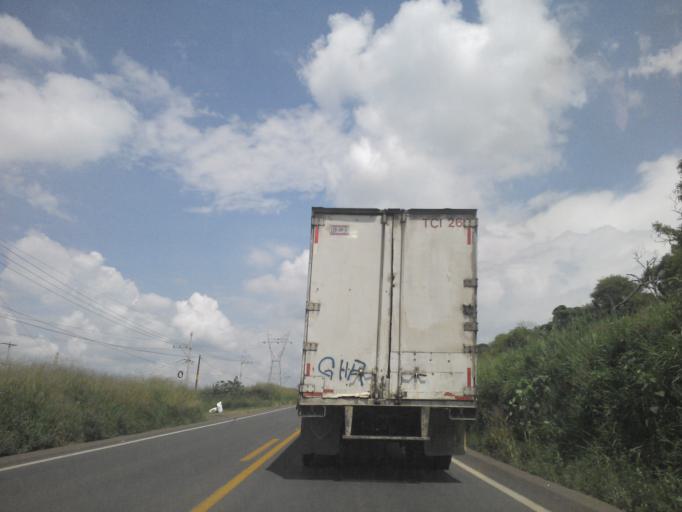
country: MX
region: Jalisco
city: Acatic
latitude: 20.7105
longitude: -102.9486
